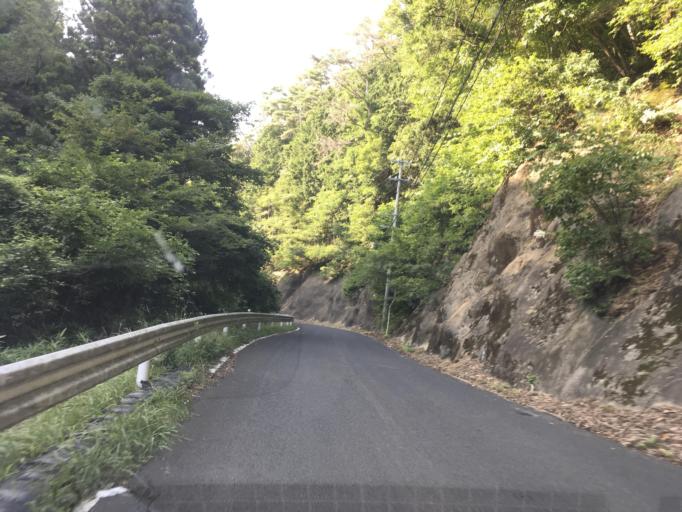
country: JP
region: Iwate
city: Ofunato
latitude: 38.9140
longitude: 141.6189
